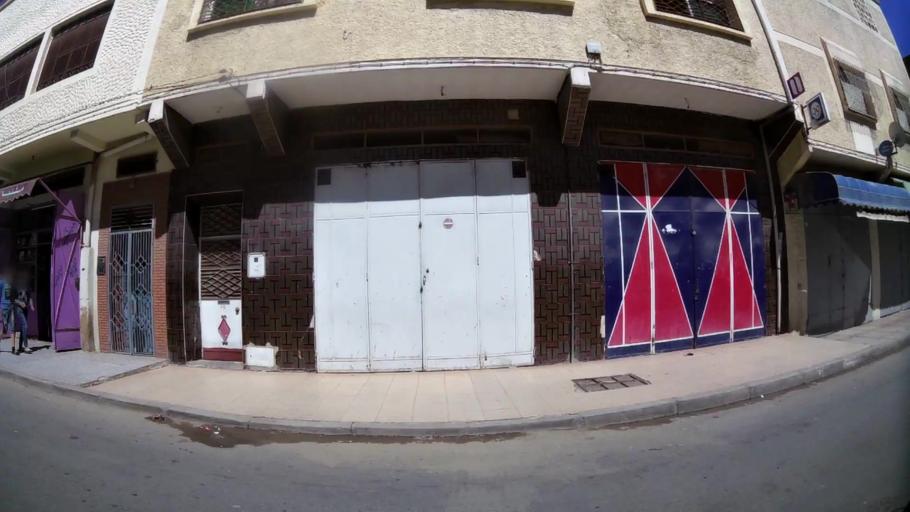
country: MA
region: Oriental
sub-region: Oujda-Angad
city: Oujda
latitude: 34.6825
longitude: -1.9320
